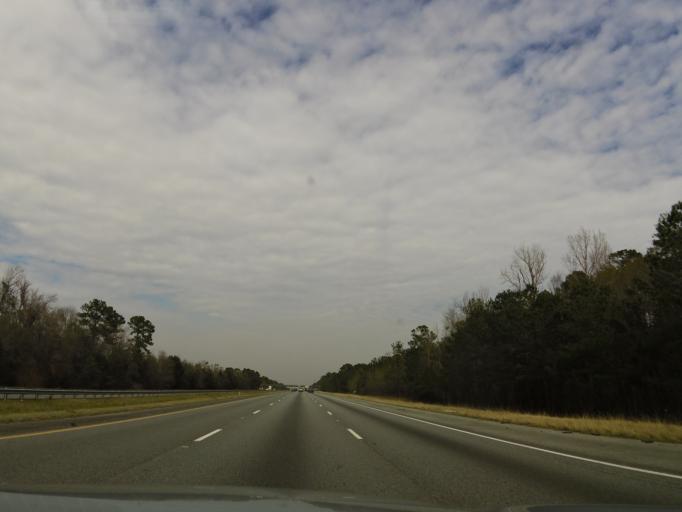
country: US
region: Georgia
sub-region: Liberty County
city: Midway
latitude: 31.6283
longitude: -81.4075
